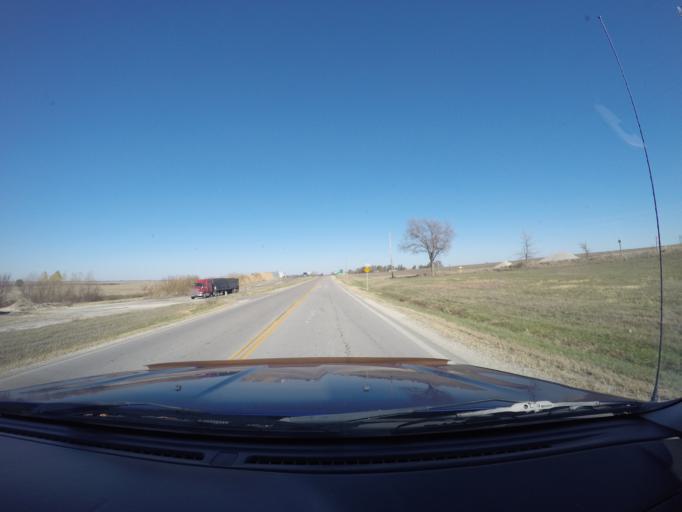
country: US
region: Kansas
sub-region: Marshall County
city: Marysville
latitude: 39.8420
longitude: -96.4171
